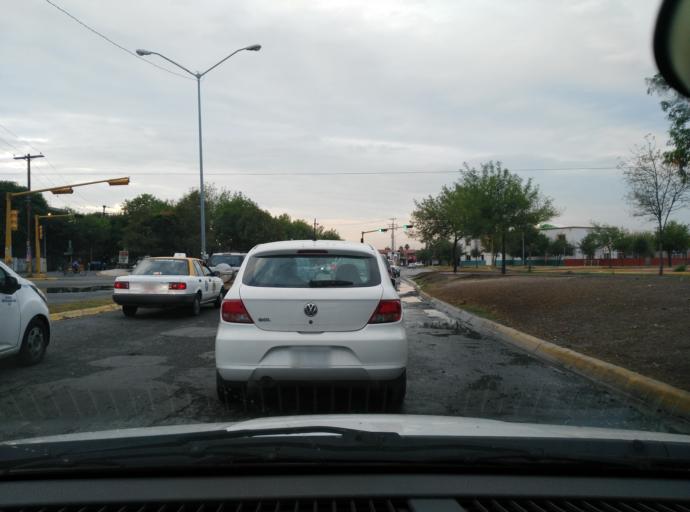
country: MX
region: Nuevo Leon
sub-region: Apodaca
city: Fraccionamiento Cosmopolis Octavo Sector
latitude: 25.7701
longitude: -100.2495
